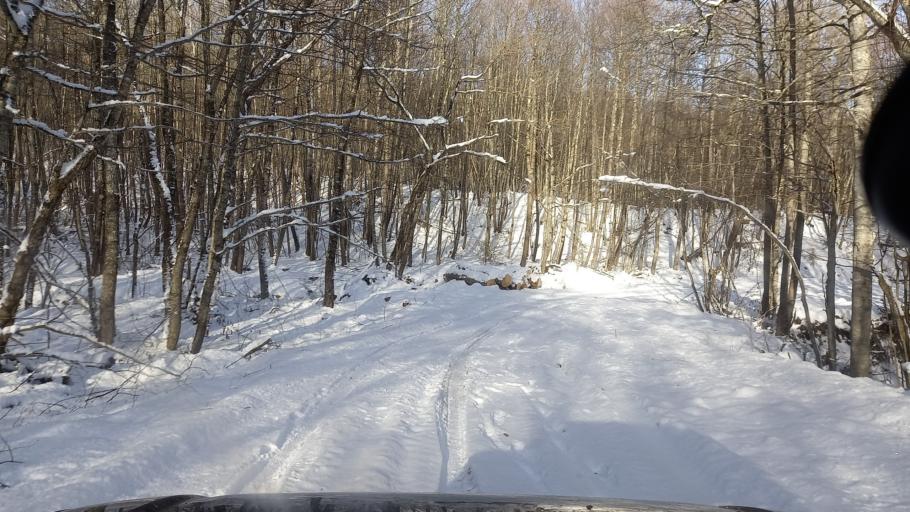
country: RU
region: Adygeya
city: Kamennomostskiy
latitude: 44.2262
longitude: 40.0935
